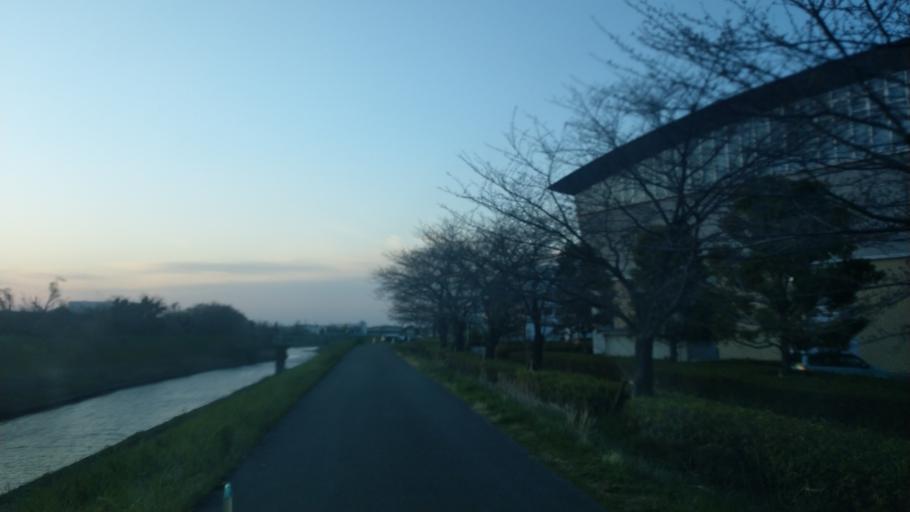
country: JP
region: Saitama
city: Shiki
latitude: 35.8551
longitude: 139.6083
